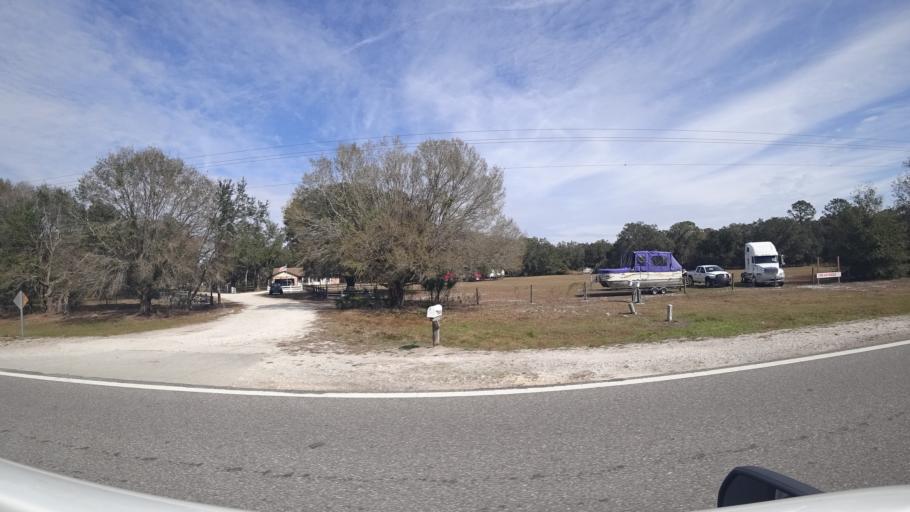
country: US
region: Florida
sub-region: Hillsborough County
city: Sun City Center
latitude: 27.5716
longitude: -82.3854
